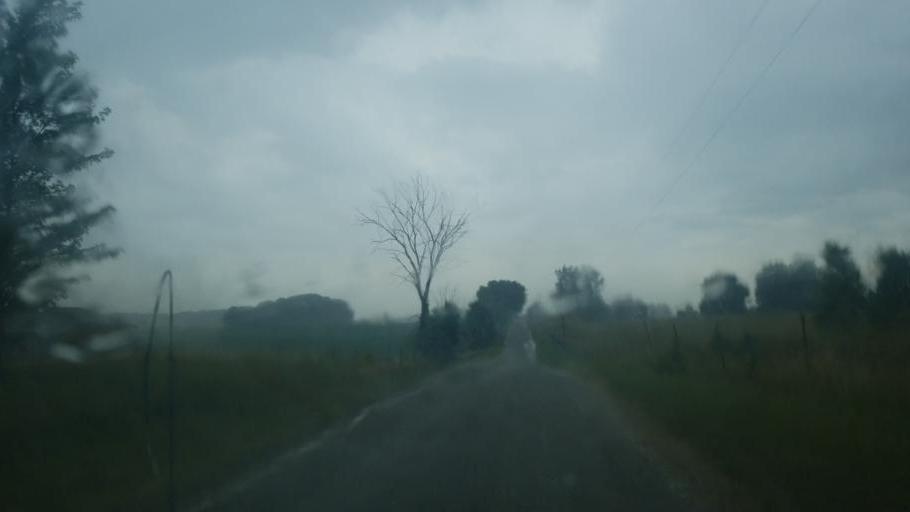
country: US
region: Indiana
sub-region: DeKalb County
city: Butler
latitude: 41.4636
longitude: -84.8279
